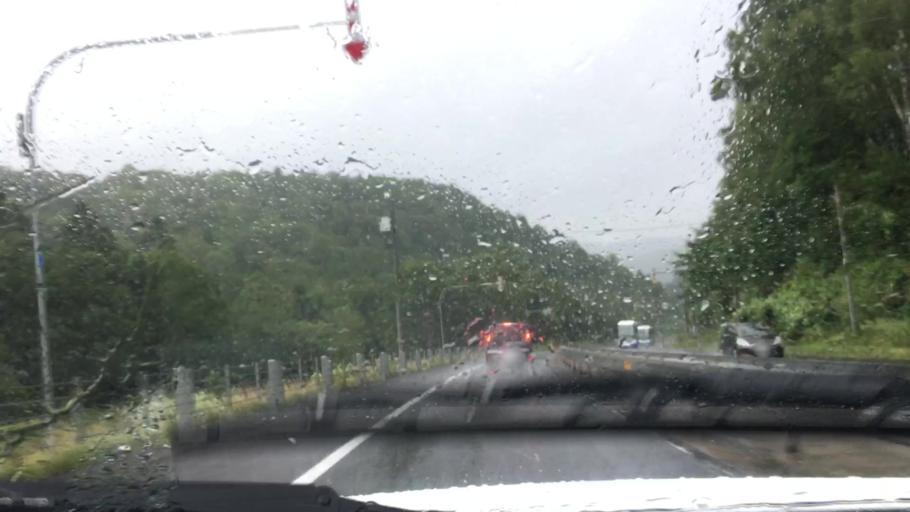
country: JP
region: Hokkaido
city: Otaru
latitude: 42.8442
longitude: 141.0602
